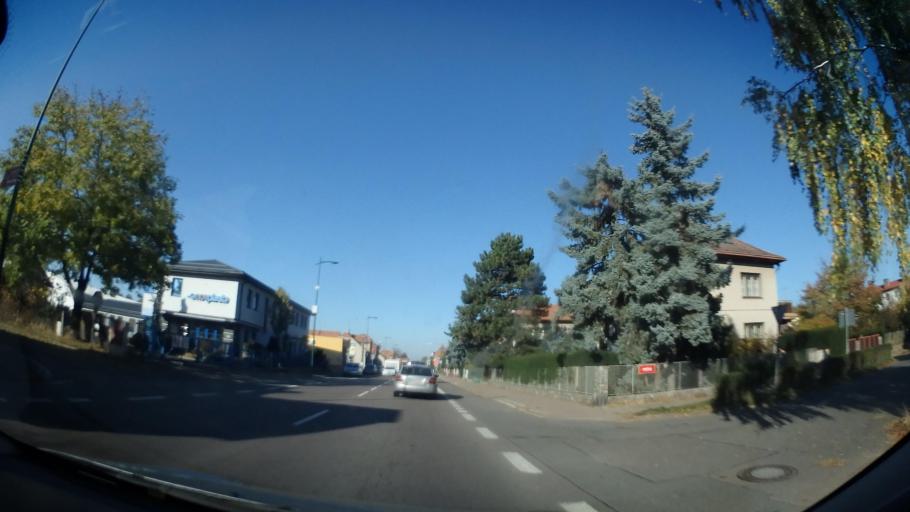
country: CZ
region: Pardubicky
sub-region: Okres Chrudim
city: Slatinany
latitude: 49.9134
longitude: 15.8175
